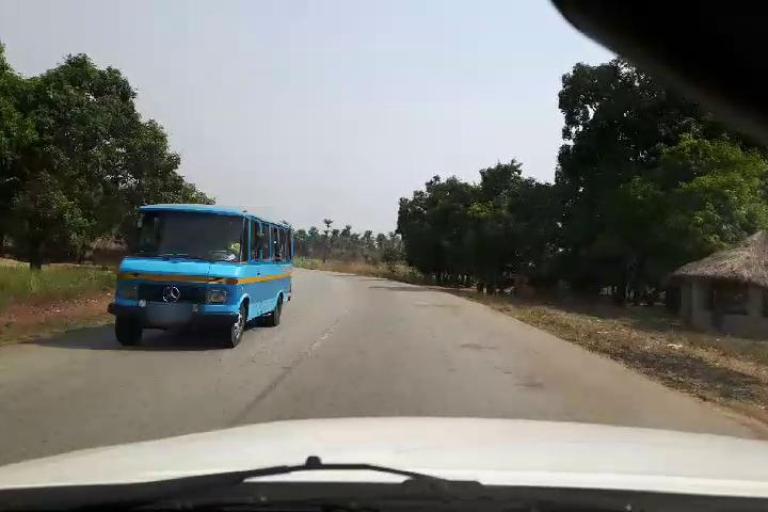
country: SL
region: Southern Province
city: Largo
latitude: 8.3105
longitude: -12.2152
